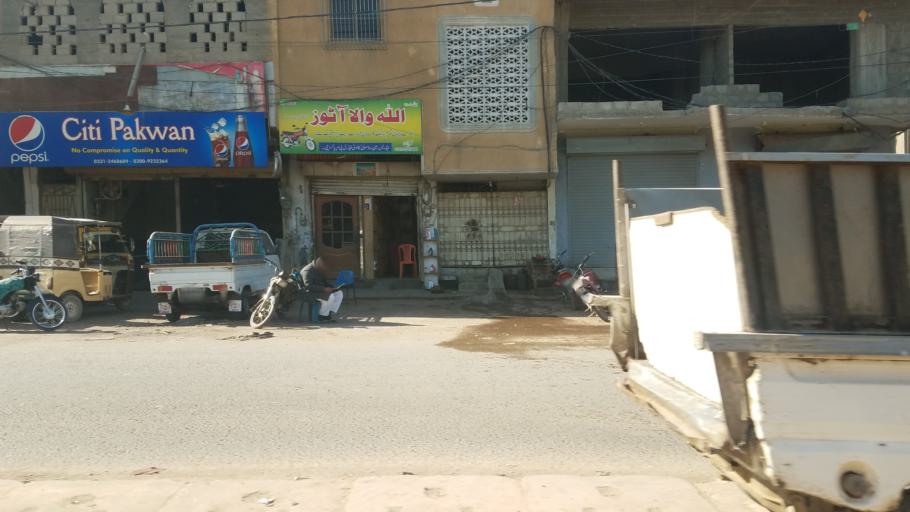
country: PK
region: Sindh
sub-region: Karachi District
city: Karachi
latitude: 24.9224
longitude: 67.0492
